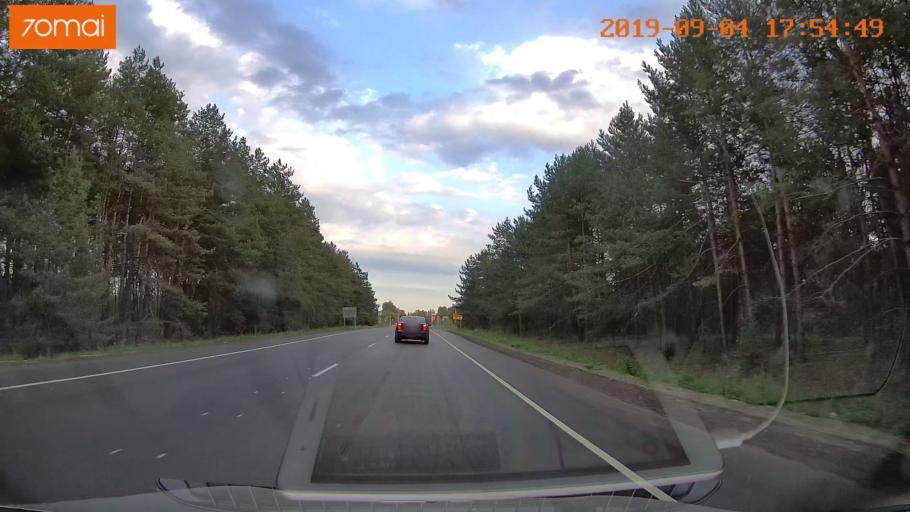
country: RU
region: Moskovskaya
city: Imeni Tsyurupy
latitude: 55.5086
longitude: 38.7552
